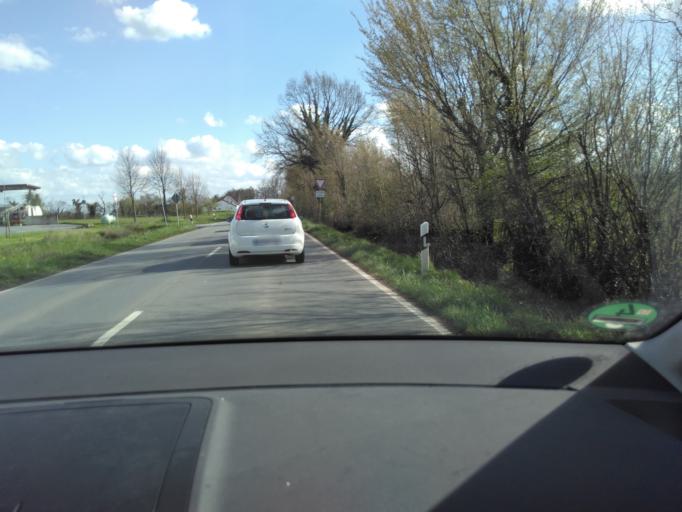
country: DE
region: North Rhine-Westphalia
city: Oelde
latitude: 51.7871
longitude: 8.1445
